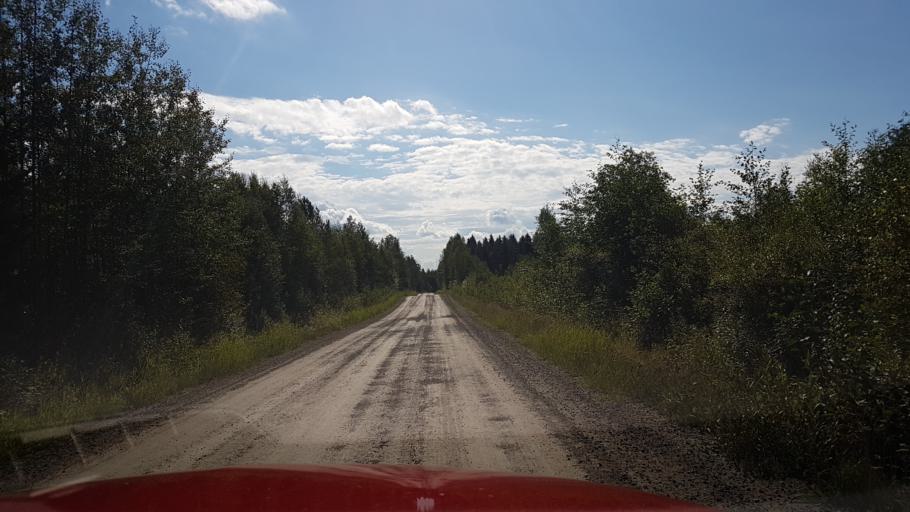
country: FI
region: Northern Ostrobothnia
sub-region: Ylivieska
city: Himanka
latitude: 64.0821
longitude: 23.7941
